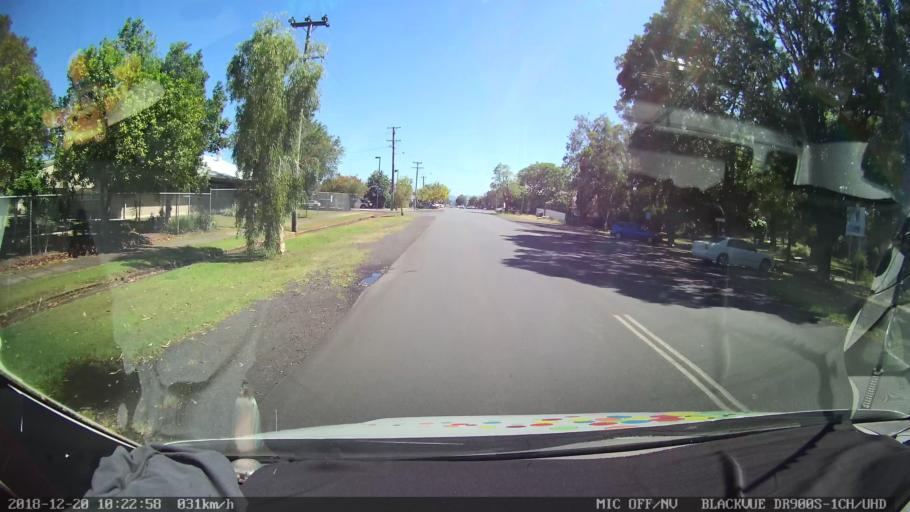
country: AU
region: New South Wales
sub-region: Richmond Valley
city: Casino
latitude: -28.8650
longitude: 153.0502
